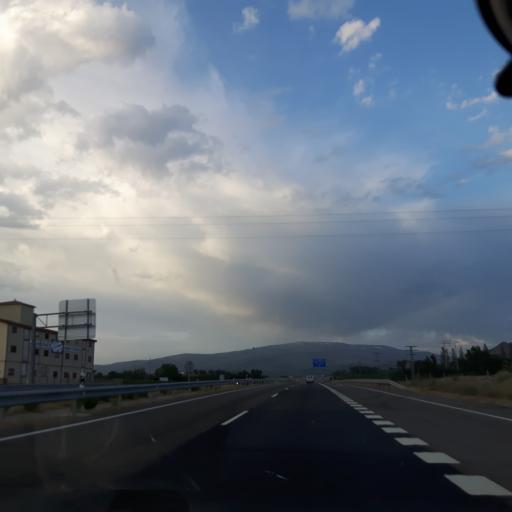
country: ES
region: Castille and Leon
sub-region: Provincia de Salamanca
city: Nava de Bejar
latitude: 40.4949
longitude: -5.6760
